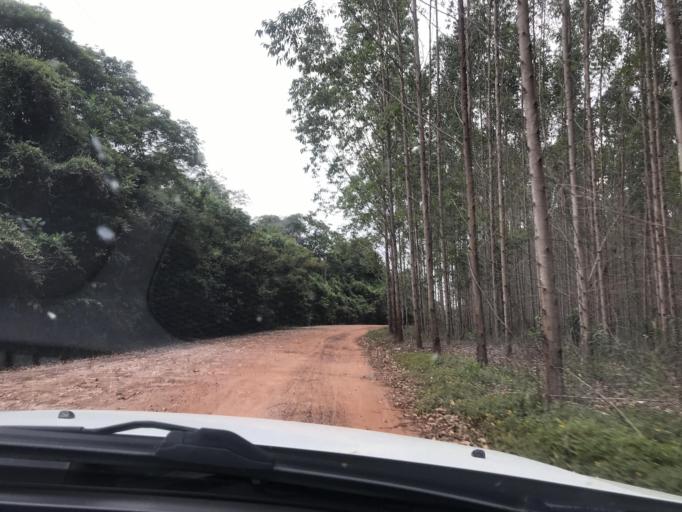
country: BR
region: Bahia
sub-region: Entre Rios
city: Entre Rios
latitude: -12.1048
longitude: -38.1877
